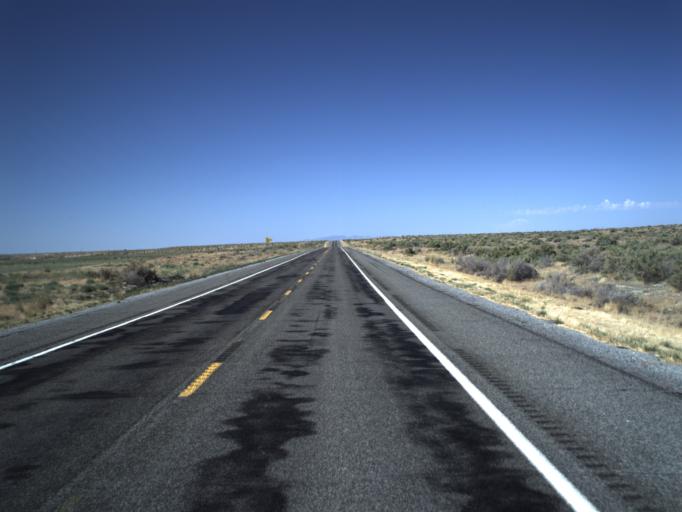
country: US
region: Utah
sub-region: Millard County
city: Delta
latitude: 39.4280
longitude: -112.4692
